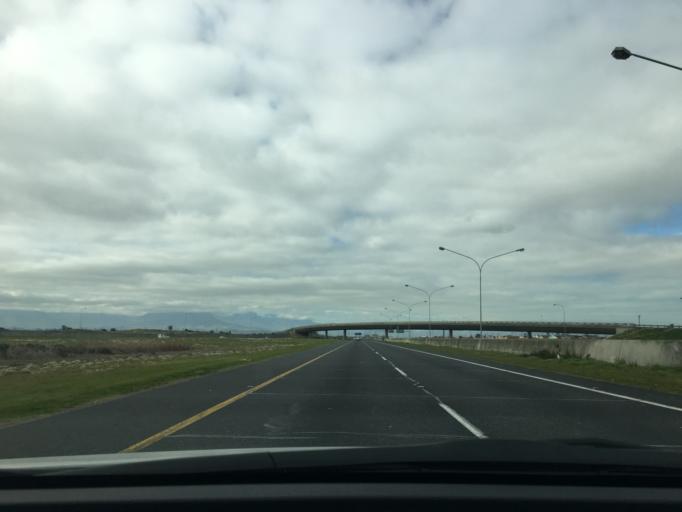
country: ZA
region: Western Cape
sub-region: City of Cape Town
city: Lansdowne
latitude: -34.0022
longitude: 18.6356
